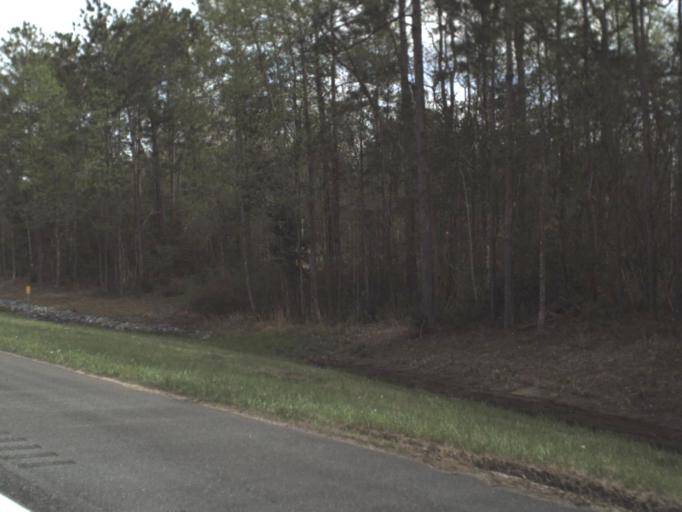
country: US
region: Florida
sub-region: Walton County
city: DeFuniak Springs
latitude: 30.6909
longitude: -86.0692
